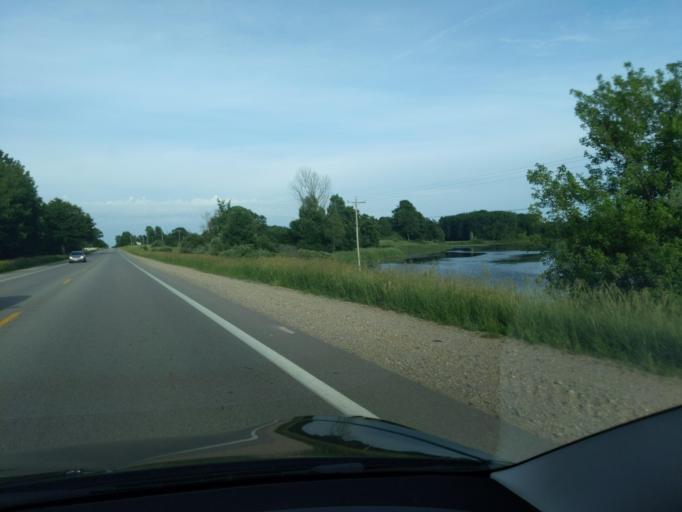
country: US
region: Michigan
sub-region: Montcalm County
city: Lakeview
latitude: 43.4313
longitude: -85.2515
